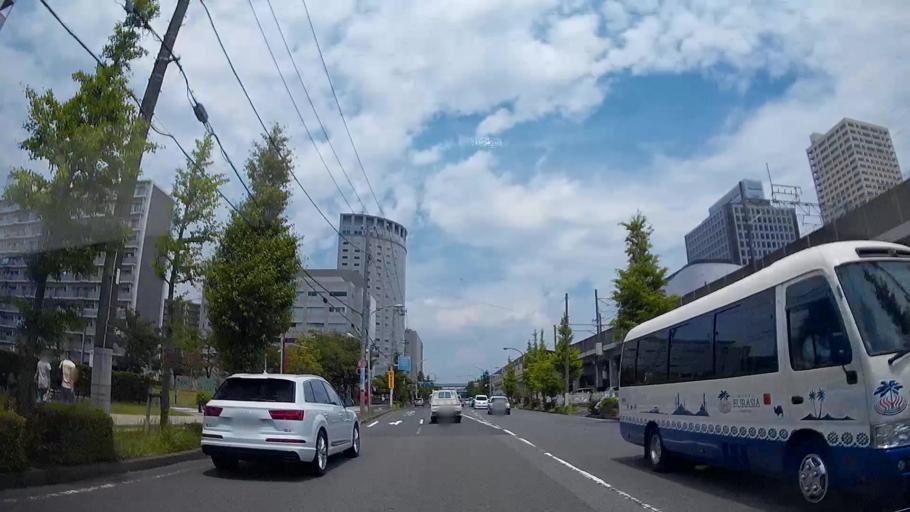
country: JP
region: Tokyo
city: Urayasu
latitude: 35.6482
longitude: 139.9103
